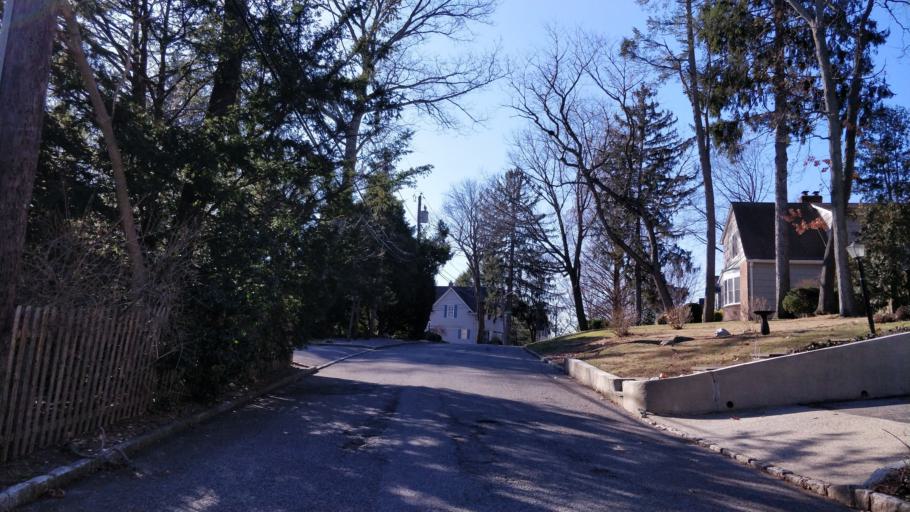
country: US
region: New York
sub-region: Nassau County
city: Glen Head
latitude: 40.8411
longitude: -73.6184
